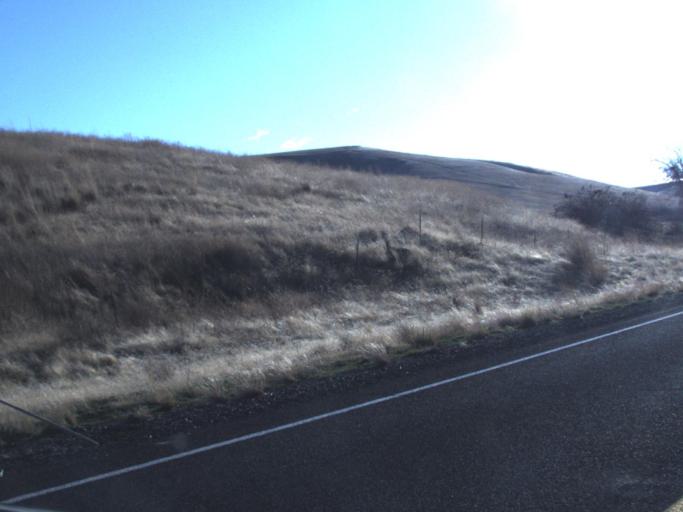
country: US
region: Washington
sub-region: Garfield County
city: Pomeroy
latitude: 46.5085
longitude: -117.7848
